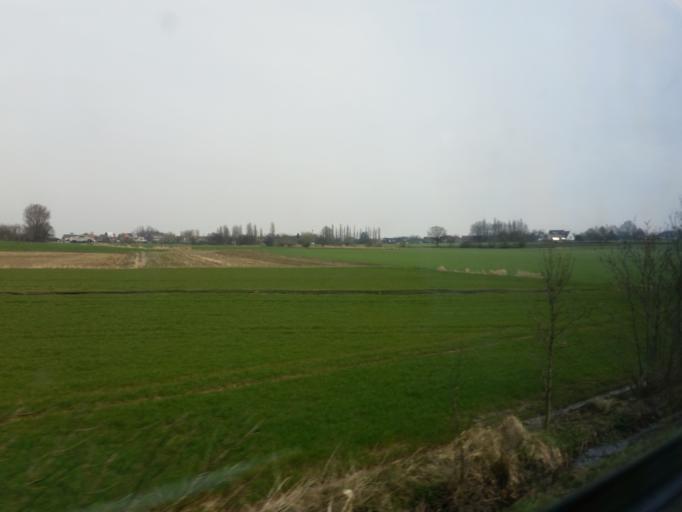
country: BE
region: Flanders
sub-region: Provincie Oost-Vlaanderen
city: Melle
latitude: 50.9826
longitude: 3.8287
